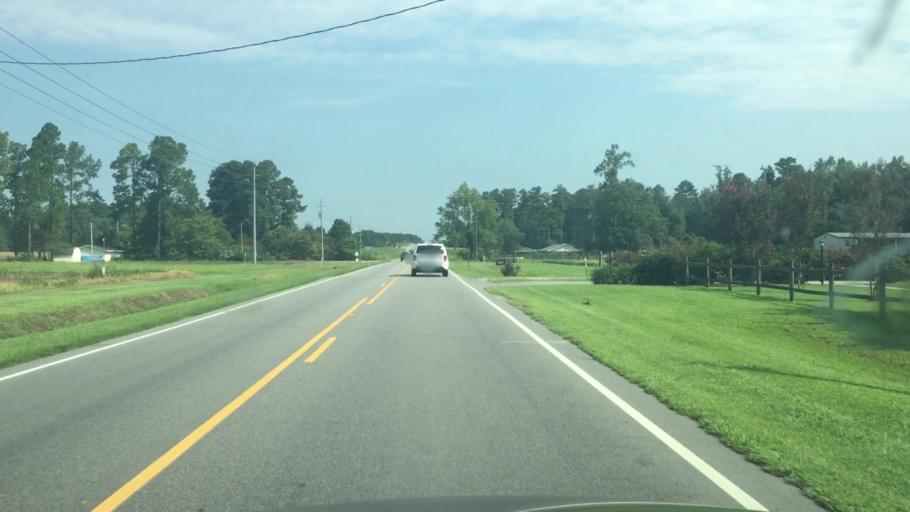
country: US
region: North Carolina
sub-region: Columbus County
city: Chadbourn
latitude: 34.3541
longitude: -78.8293
